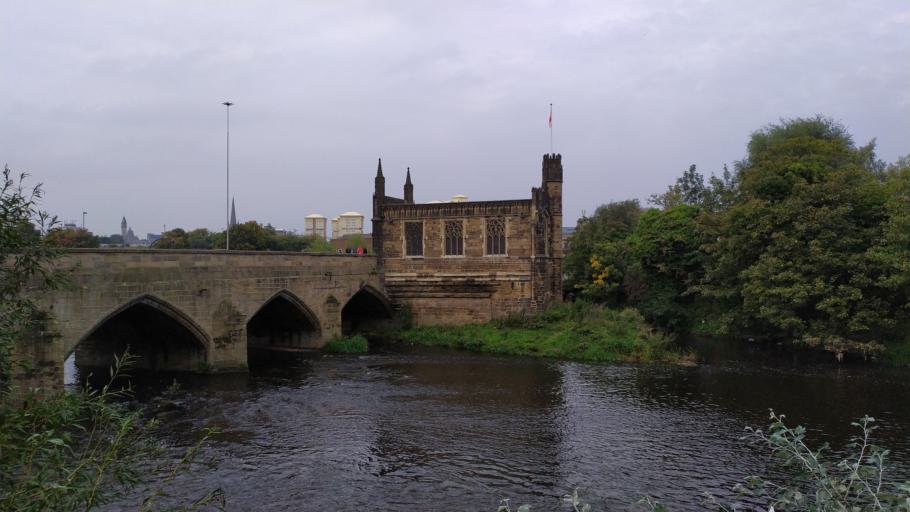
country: GB
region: England
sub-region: City and Borough of Wakefield
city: Wakefield
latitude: 53.6762
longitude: -1.4892
